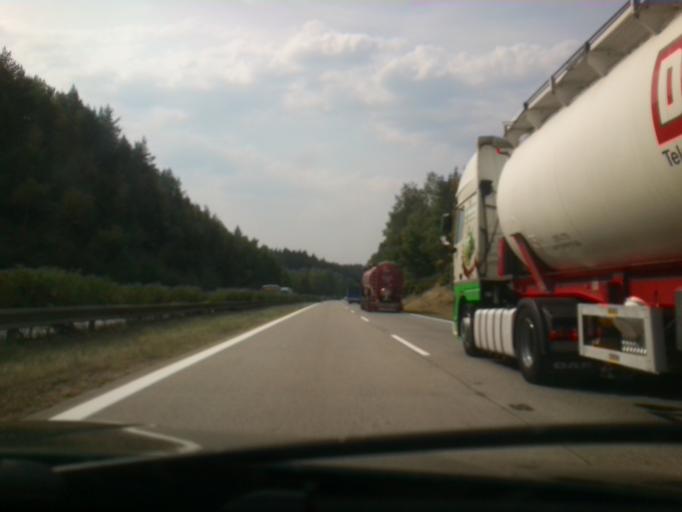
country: CZ
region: Central Bohemia
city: Divisov
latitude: 49.8078
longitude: 14.8919
